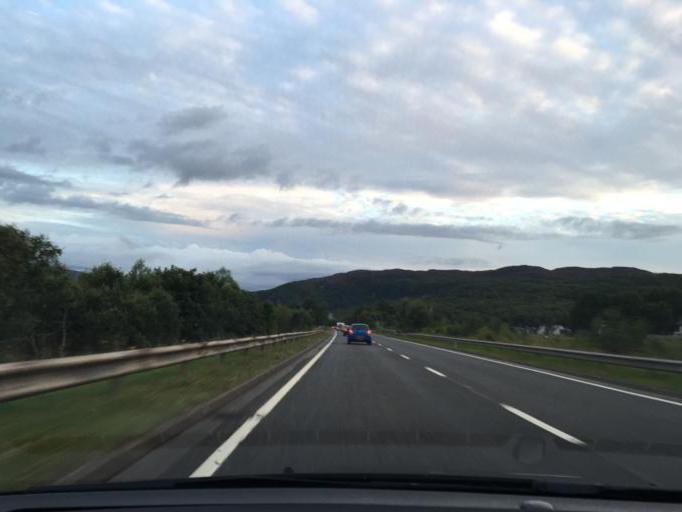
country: GB
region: Scotland
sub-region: Highland
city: Aviemore
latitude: 57.2049
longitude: -3.8317
